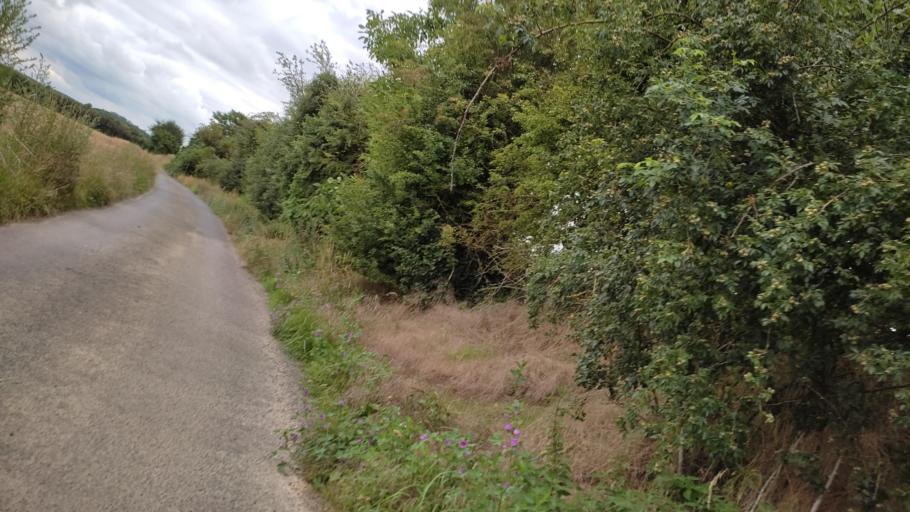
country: FR
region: Nord-Pas-de-Calais
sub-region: Departement du Pas-de-Calais
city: Beaumetz-les-Loges
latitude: 50.2626
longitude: 2.6617
